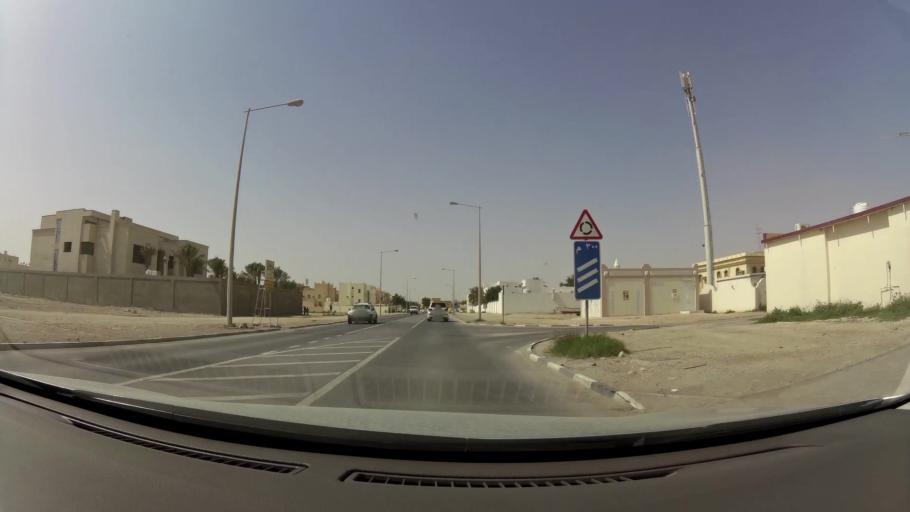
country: QA
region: Baladiyat Umm Salal
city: Umm Salal Muhammad
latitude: 25.3959
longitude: 51.4263
